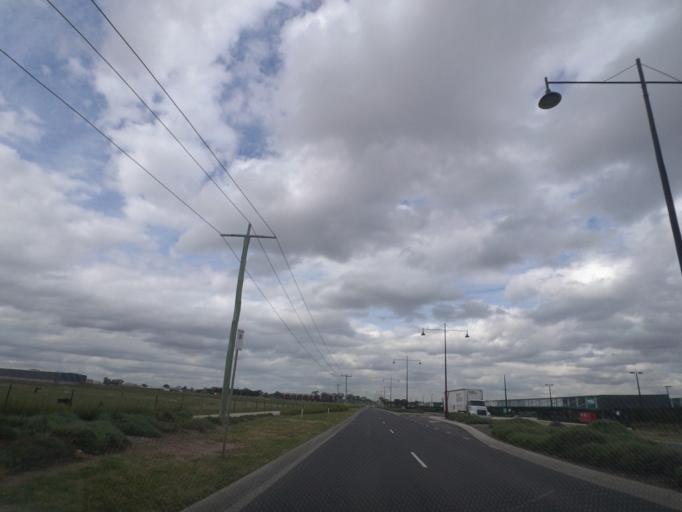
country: AU
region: Victoria
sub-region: Hume
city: Tullamarine
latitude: -37.6929
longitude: 144.8591
